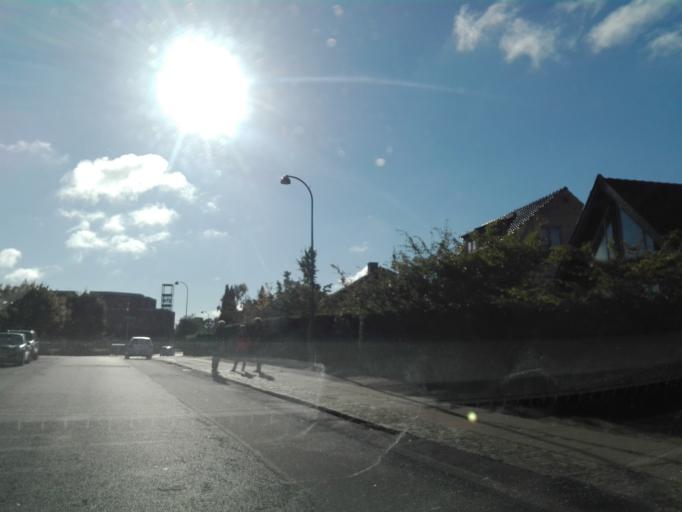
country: DK
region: Capital Region
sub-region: Lyngby-Tarbaek Kommune
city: Kongens Lyngby
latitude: 55.7481
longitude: 12.5195
